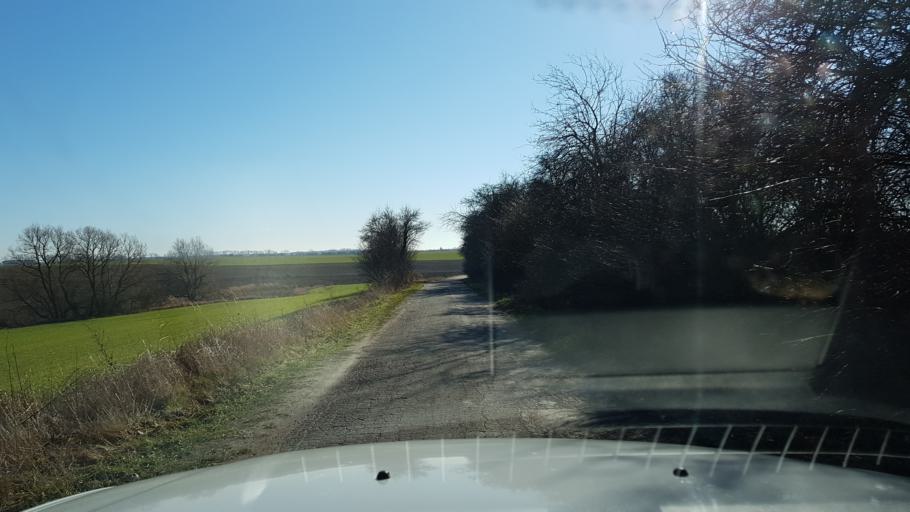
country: PL
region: West Pomeranian Voivodeship
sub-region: Powiat pyrzycki
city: Przelewice
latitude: 53.0455
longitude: 15.0623
